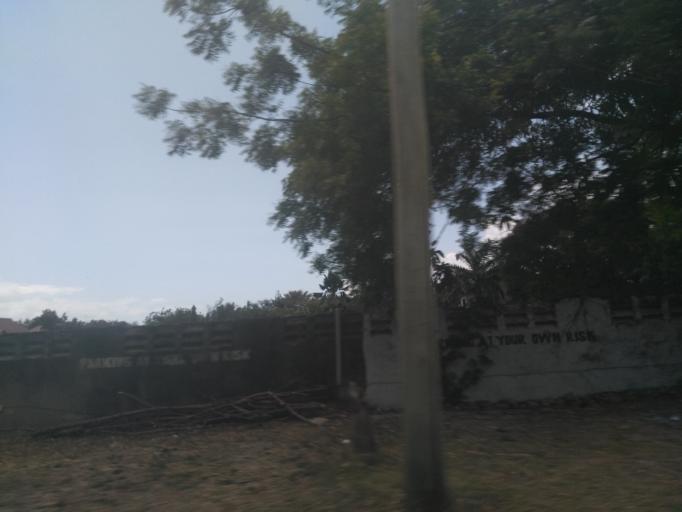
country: TZ
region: Dar es Salaam
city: Magomeni
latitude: -6.7463
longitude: 39.2795
